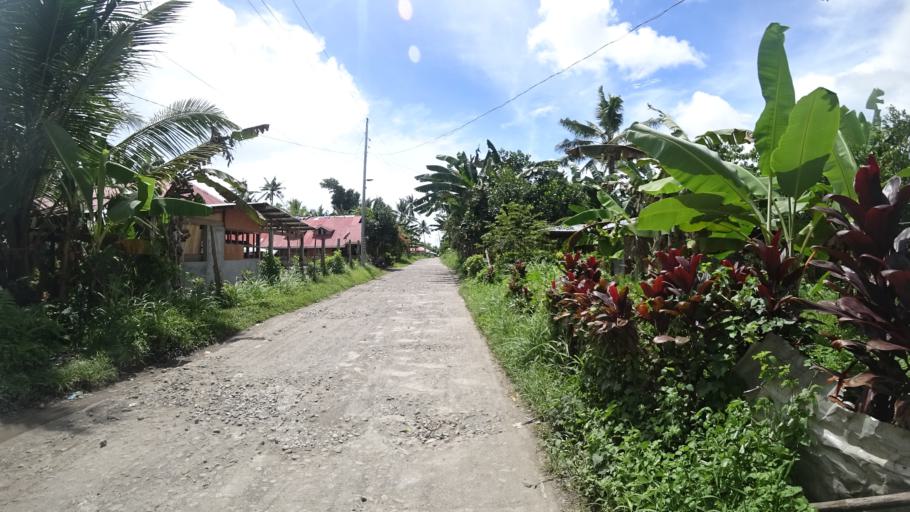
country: PH
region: Eastern Visayas
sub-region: Province of Leyte
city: Alangalang
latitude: 11.2313
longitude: 124.8431
